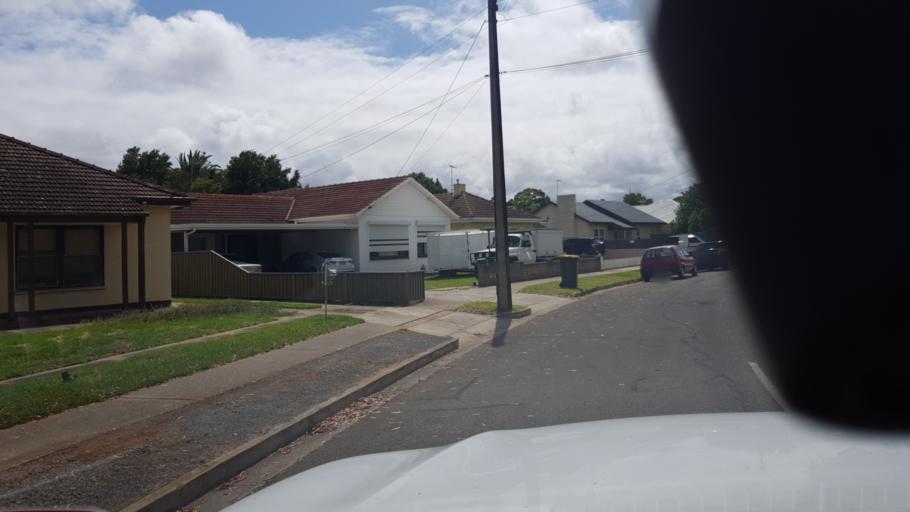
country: AU
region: South Australia
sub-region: Adelaide
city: Brighton
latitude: -35.0201
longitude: 138.5286
